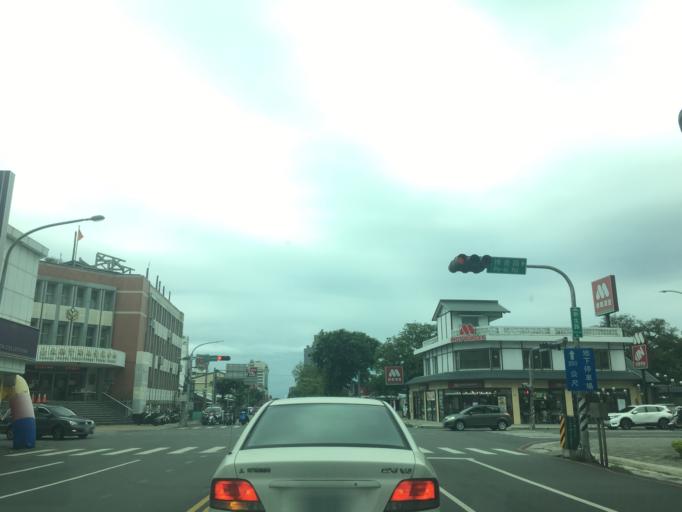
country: TW
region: Taiwan
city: Taitung City
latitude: 22.7547
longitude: 121.1457
